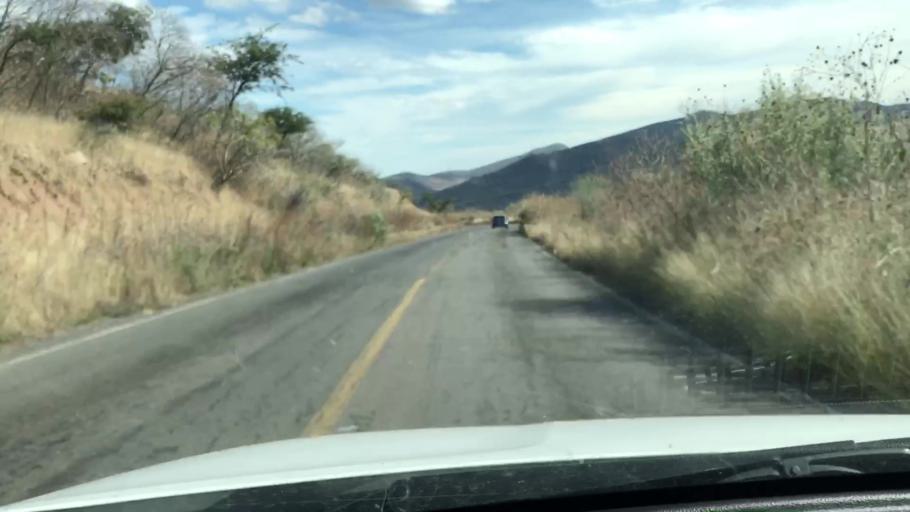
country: MX
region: Jalisco
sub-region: Zacoalco de Torres
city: Barranca de Otates (Barranca de Otatan)
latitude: 20.2451
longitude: -103.6703
